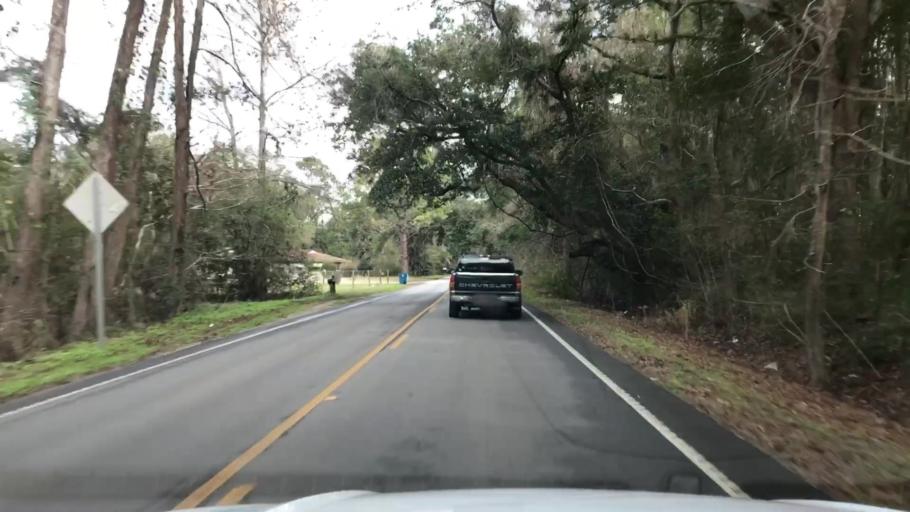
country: US
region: South Carolina
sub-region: Charleston County
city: Kiawah Island
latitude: 32.6793
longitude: -80.0324
